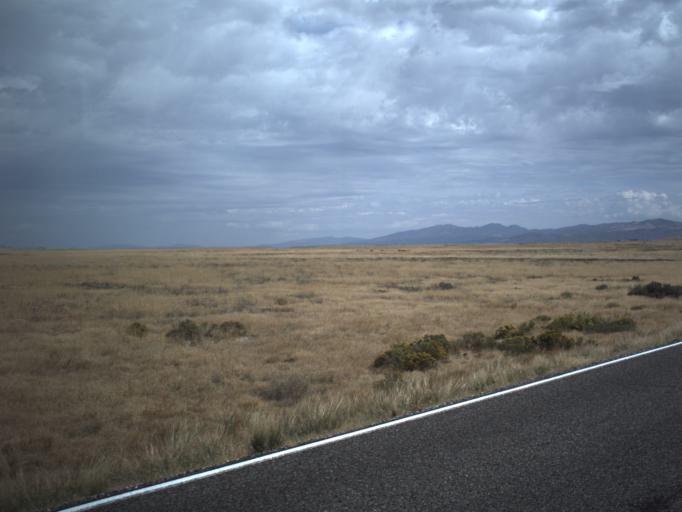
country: US
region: Utah
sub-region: Tooele County
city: Wendover
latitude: 41.4010
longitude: -113.9501
